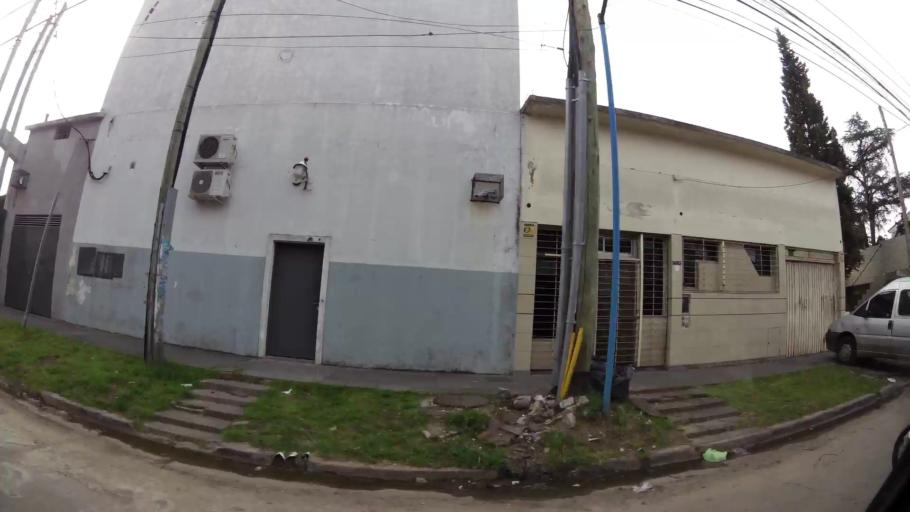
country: AR
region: Buenos Aires
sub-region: Partido de Quilmes
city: Quilmes
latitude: -34.7516
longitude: -58.2847
